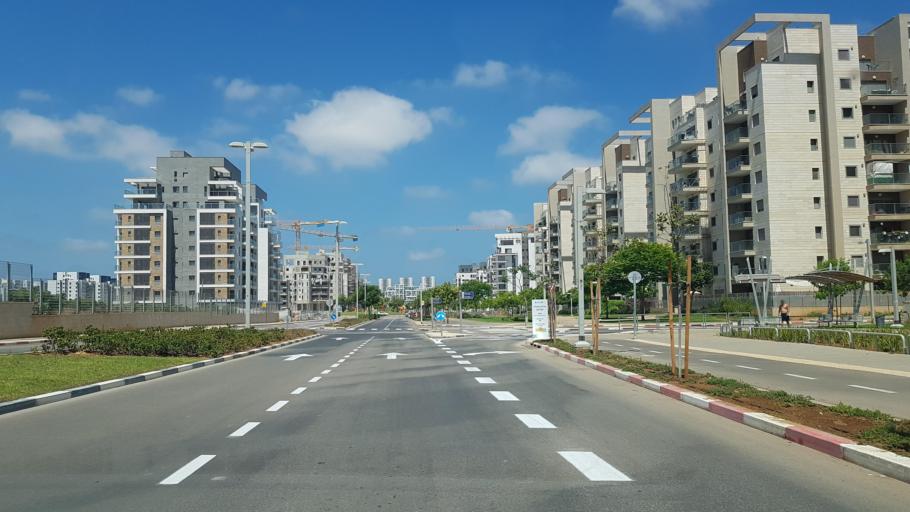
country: IL
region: Tel Aviv
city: Herzliyya
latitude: 32.1607
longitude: 34.8295
